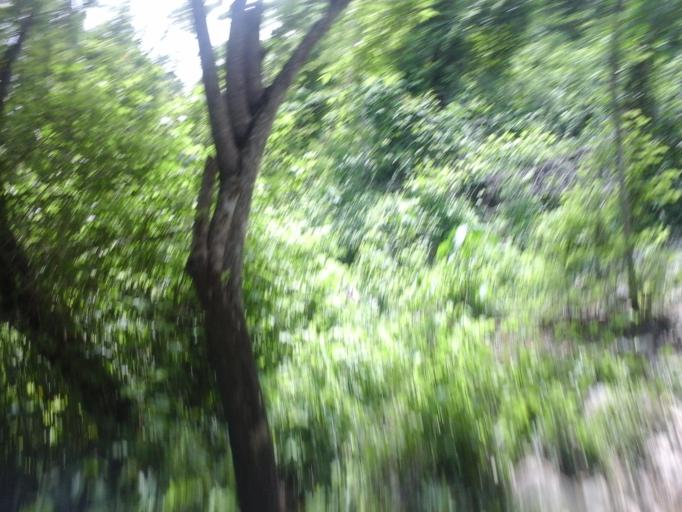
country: CO
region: Cesar
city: Becerril
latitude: 9.7478
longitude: -73.1642
